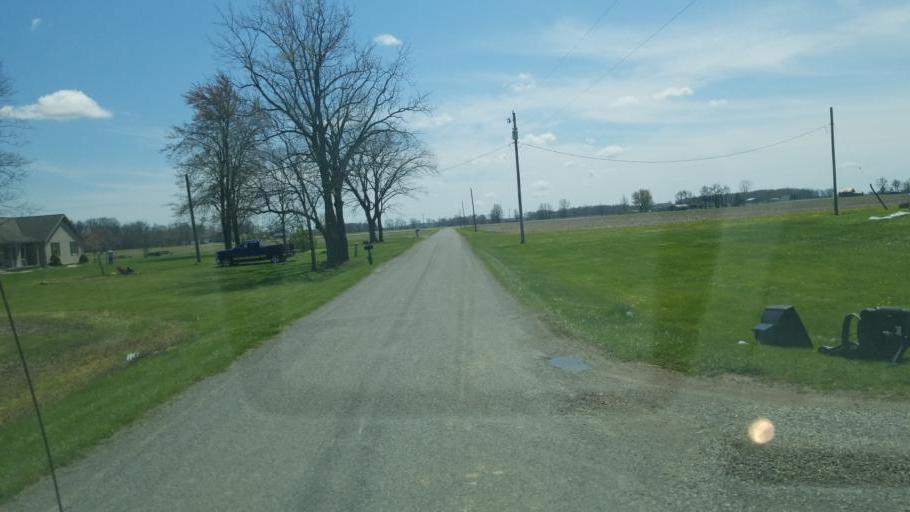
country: US
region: Ohio
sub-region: Union County
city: Richwood
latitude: 40.5036
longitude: -83.2901
